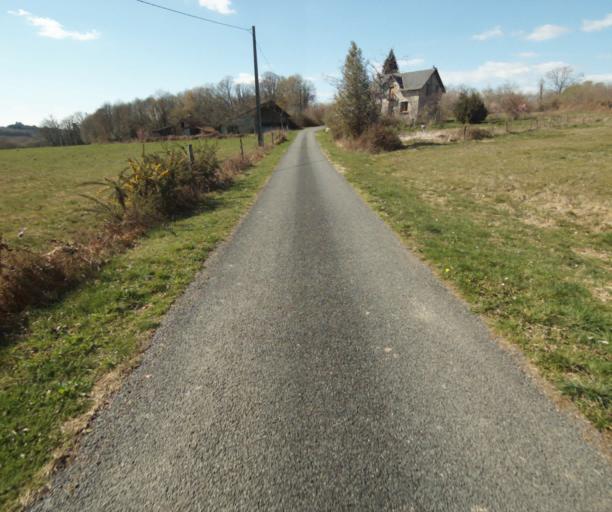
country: FR
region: Limousin
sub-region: Departement de la Correze
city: Saint-Mexant
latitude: 45.2866
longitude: 1.6835
